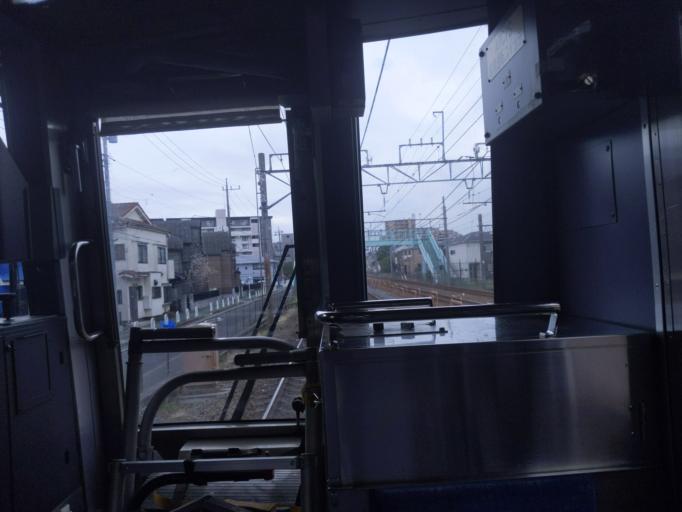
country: JP
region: Saitama
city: Soka
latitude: 35.7856
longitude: 139.7875
